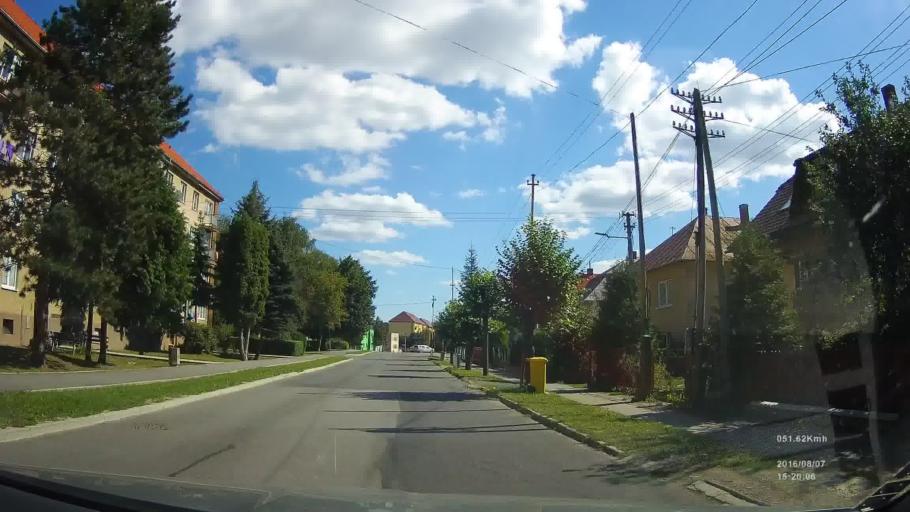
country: SK
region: Presovsky
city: Stropkov
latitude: 49.2047
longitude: 21.6475
